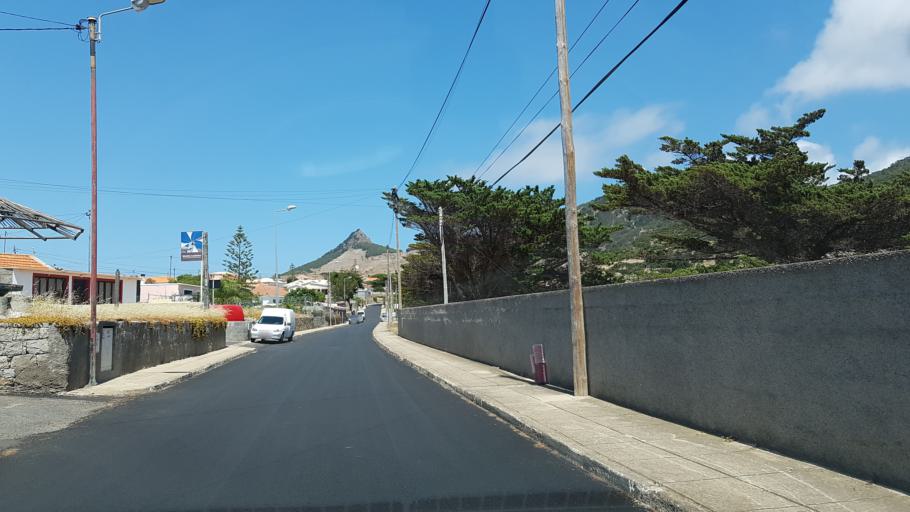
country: PT
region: Madeira
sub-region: Porto Santo
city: Camacha
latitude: 33.0861
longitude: -16.3449
